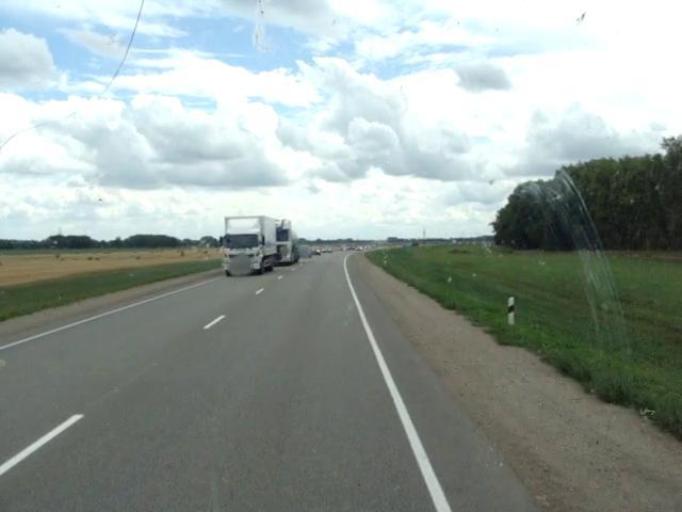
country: RU
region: Altai Krai
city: Shubenka
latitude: 52.6843
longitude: 85.0434
